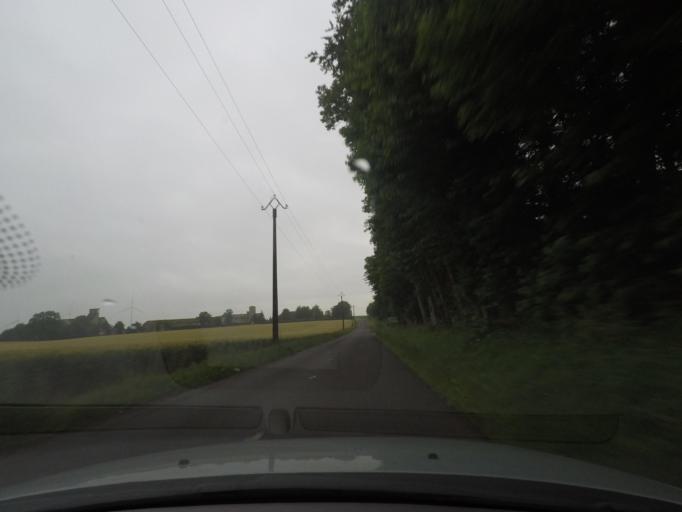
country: FR
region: Haute-Normandie
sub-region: Departement de la Seine-Maritime
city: Saint-Martin-Osmonville
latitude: 49.6150
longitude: 1.2485
